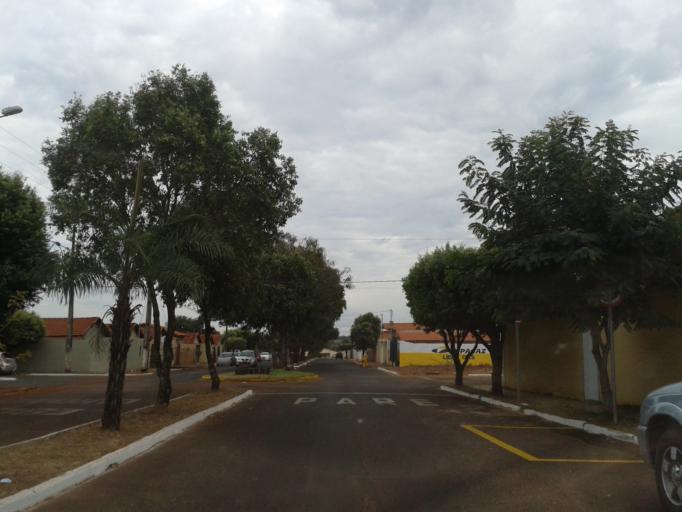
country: BR
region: Minas Gerais
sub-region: Santa Vitoria
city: Santa Vitoria
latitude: -18.8523
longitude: -50.1257
